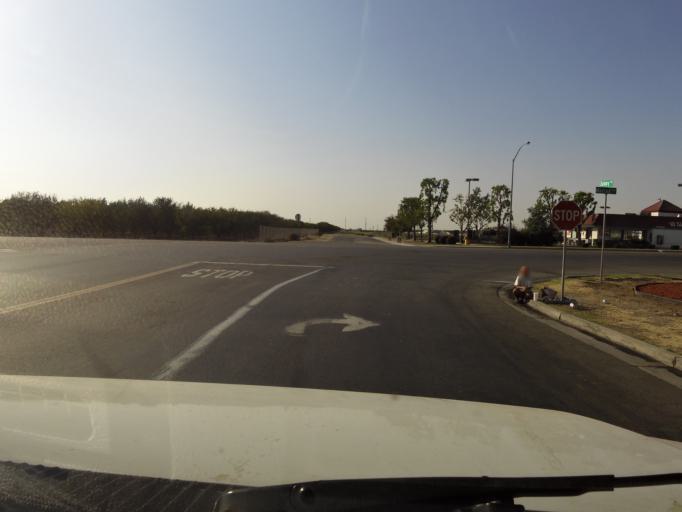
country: US
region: California
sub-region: Kern County
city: Shafter
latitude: 35.5300
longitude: -119.1871
